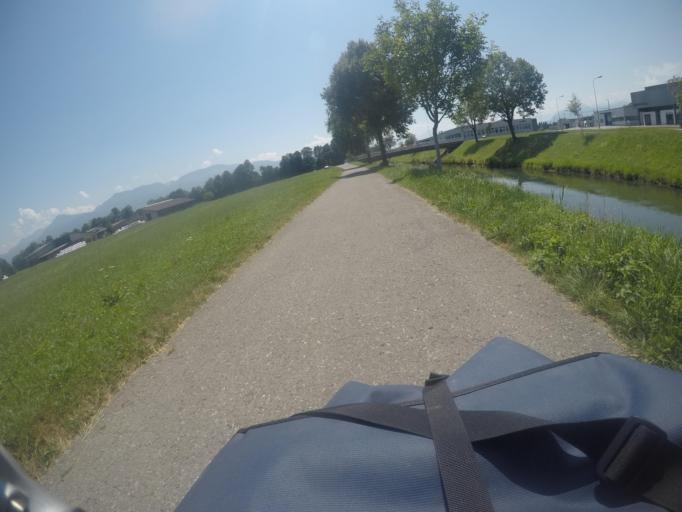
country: CH
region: Saint Gallen
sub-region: Wahlkreis Rheintal
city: Au
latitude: 47.4250
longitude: 9.6398
